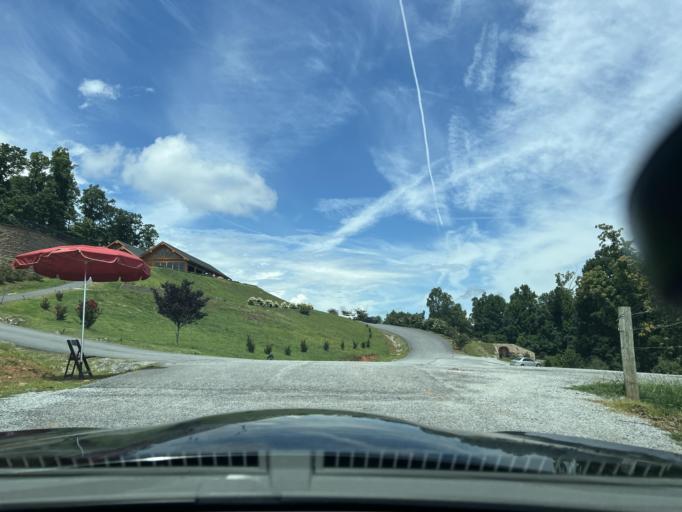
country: US
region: North Carolina
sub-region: Henderson County
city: Edneyville
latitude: 35.3894
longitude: -82.3075
